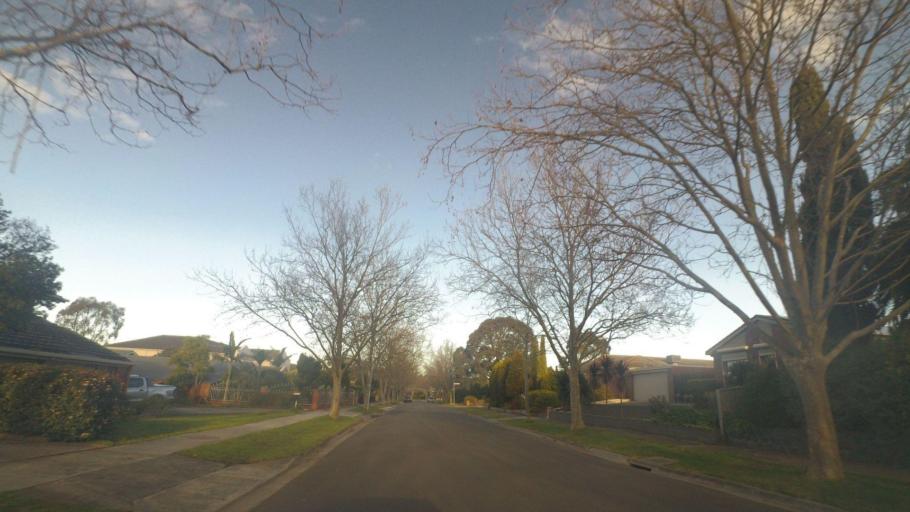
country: AU
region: Victoria
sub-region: Knox
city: Scoresby
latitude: -37.9147
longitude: 145.2387
